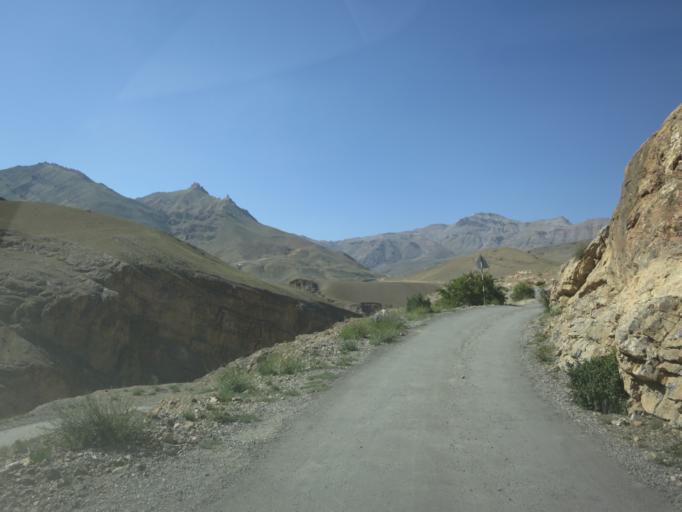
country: IN
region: Himachal Pradesh
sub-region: Kulu
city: Manali
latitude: 32.3224
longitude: 78.0013
